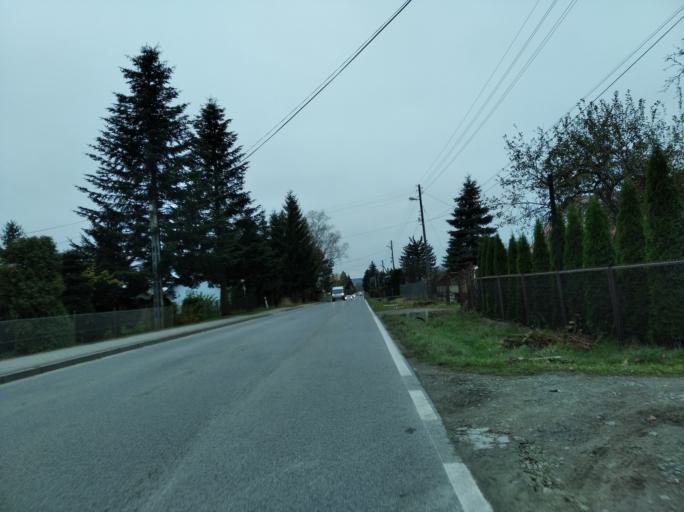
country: PL
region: Subcarpathian Voivodeship
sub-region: Powiat krosnienski
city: Chorkowka
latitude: 49.6751
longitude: 21.7025
